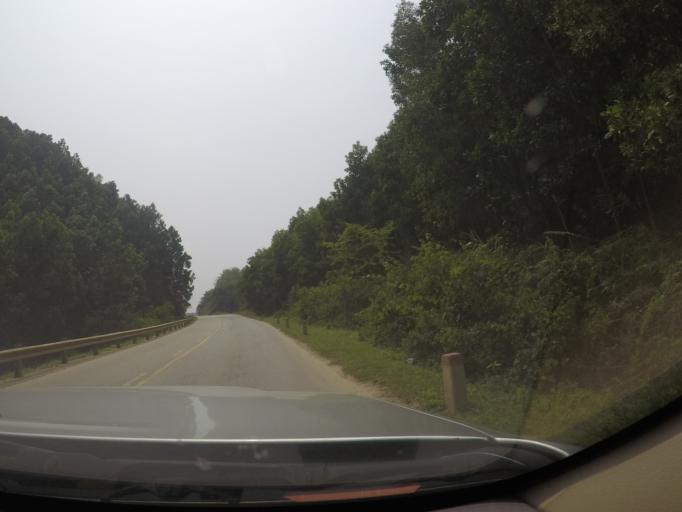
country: VN
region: Thanh Hoa
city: Thi Tran Thuong Xuan
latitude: 19.8405
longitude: 105.4003
